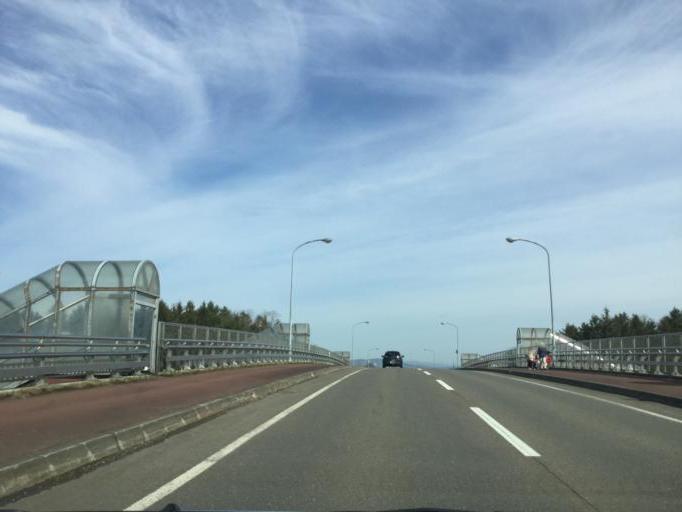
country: JP
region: Hokkaido
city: Iwamizawa
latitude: 43.1771
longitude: 141.7078
